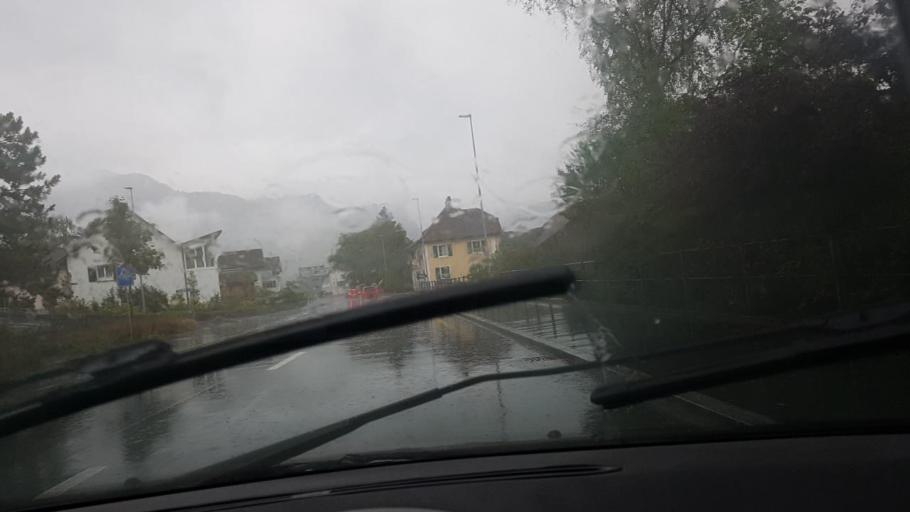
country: LI
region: Balzers
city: Balzers
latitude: 47.0728
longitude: 9.5093
